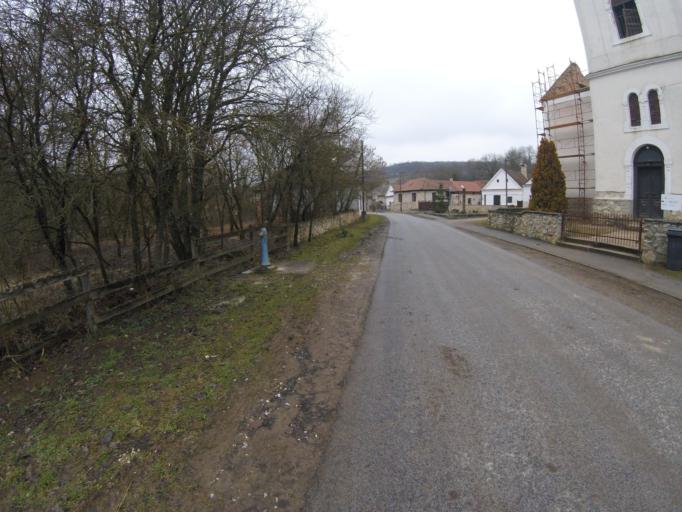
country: HU
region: Borsod-Abauj-Zemplen
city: Rudabanya
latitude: 48.4433
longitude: 20.5870
